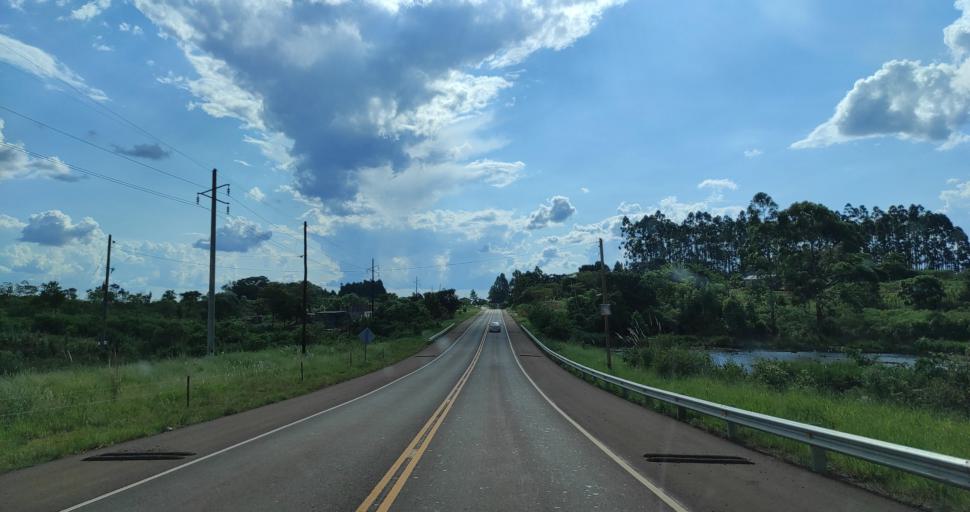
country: AR
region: Misiones
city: Bernardo de Irigoyen
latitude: -26.2952
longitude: -53.7826
